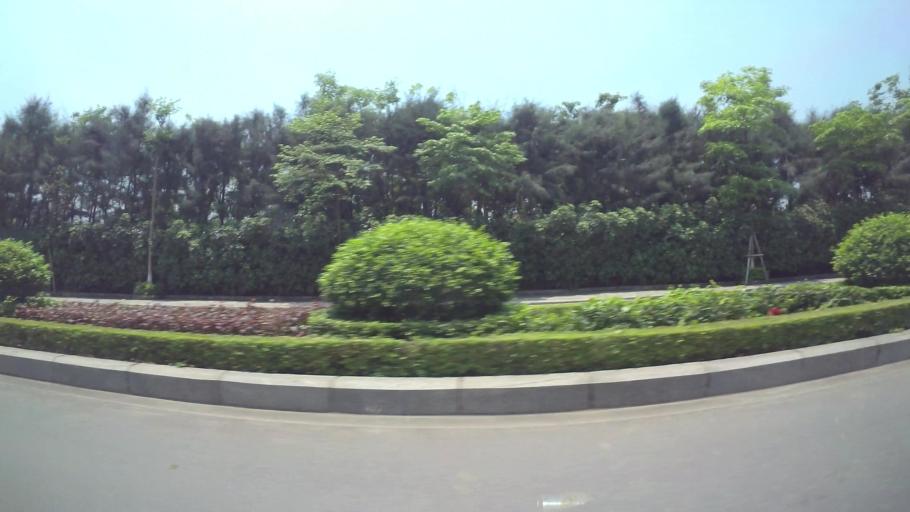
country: VN
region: Ha Noi
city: Trau Quy
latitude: 21.0349
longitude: 105.8958
